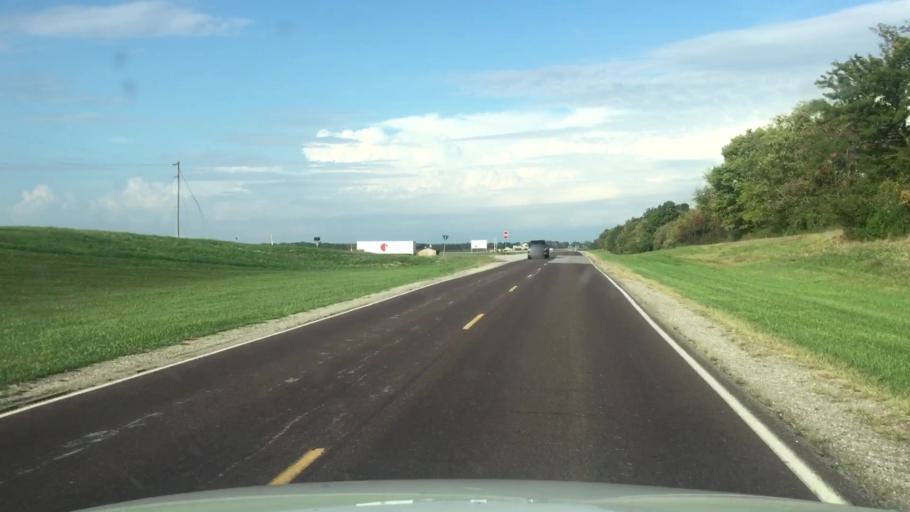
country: US
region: Missouri
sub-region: Boone County
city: Ashland
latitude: 38.8320
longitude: -92.2306
